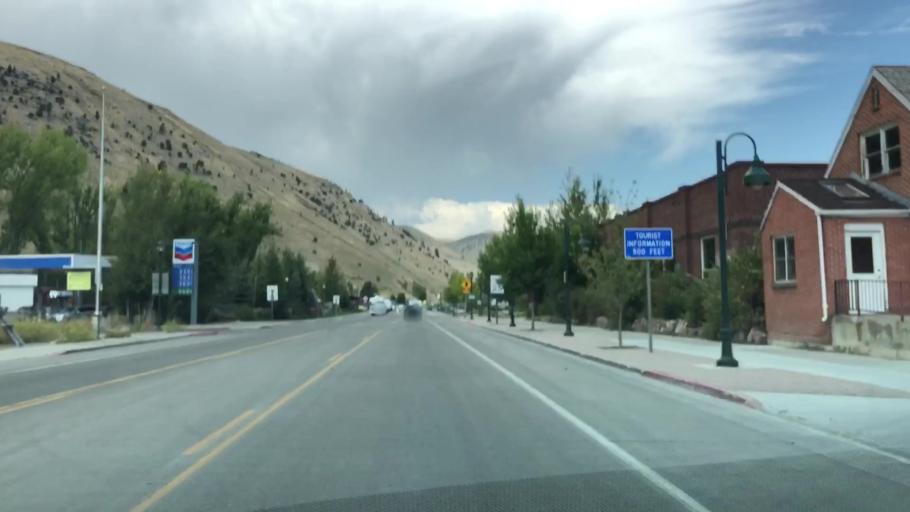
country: US
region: Wyoming
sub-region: Teton County
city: Jackson
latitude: 43.4844
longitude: -110.7623
